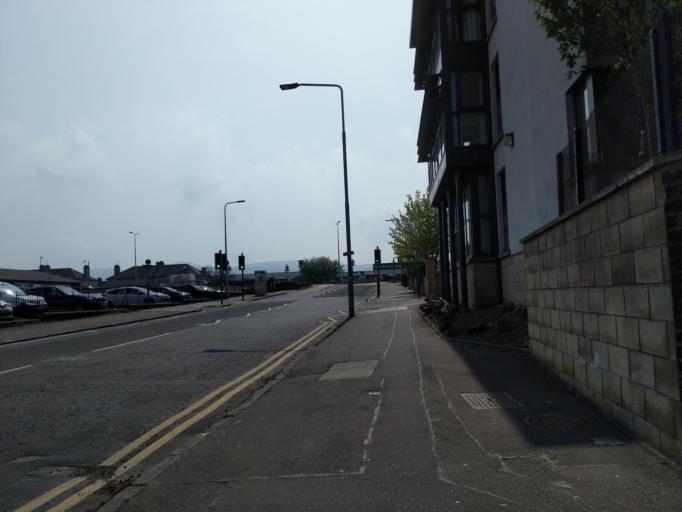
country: GB
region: Scotland
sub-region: Edinburgh
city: Currie
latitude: 55.9238
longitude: -3.2873
